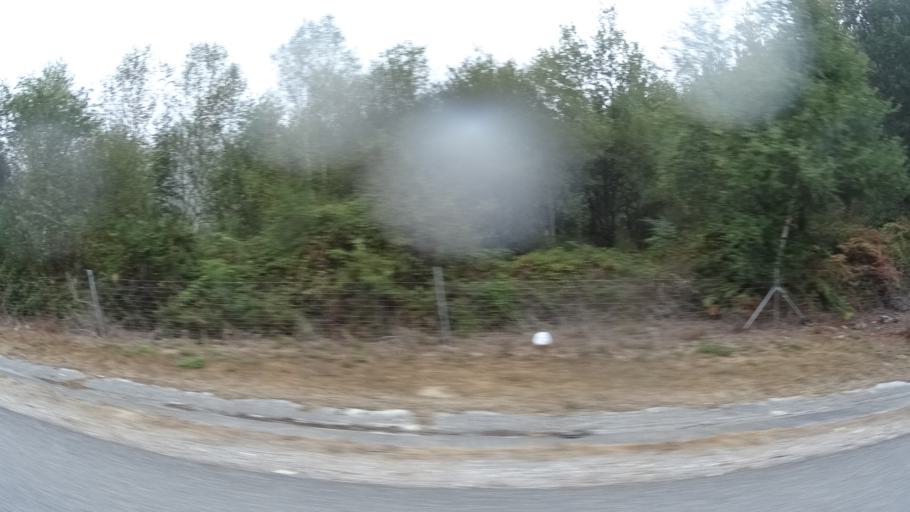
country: ES
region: Galicia
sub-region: Provincia de Lugo
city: Corgo
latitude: 42.9616
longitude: -7.4488
